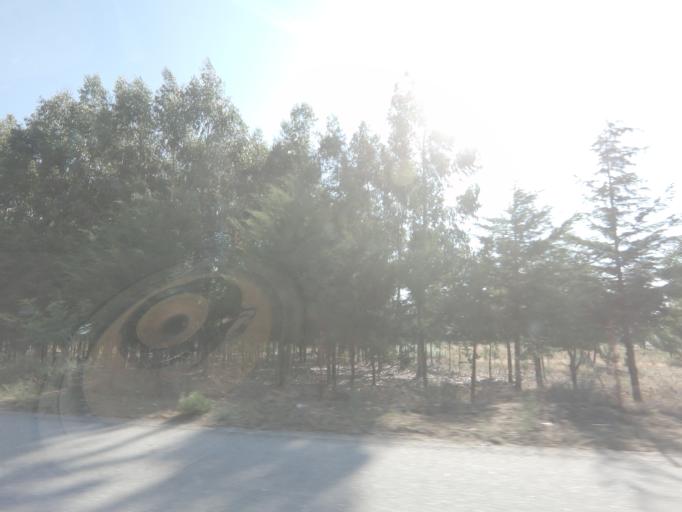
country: PT
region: Viseu
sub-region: Moimenta da Beira
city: Moimenta da Beira
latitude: 41.0375
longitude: -7.5690
